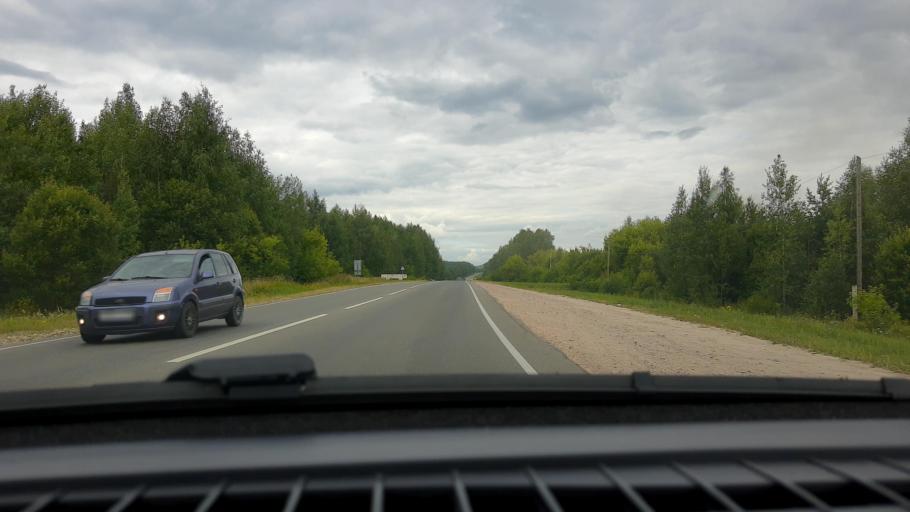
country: RU
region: Nizjnij Novgorod
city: Sergach
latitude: 55.5648
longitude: 45.3957
